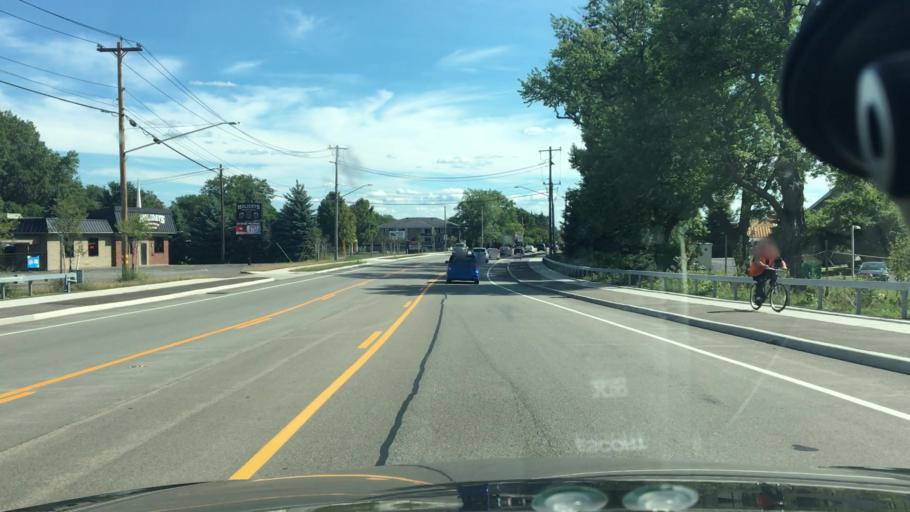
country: US
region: New York
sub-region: Erie County
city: West Seneca
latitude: 42.8692
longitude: -78.7873
